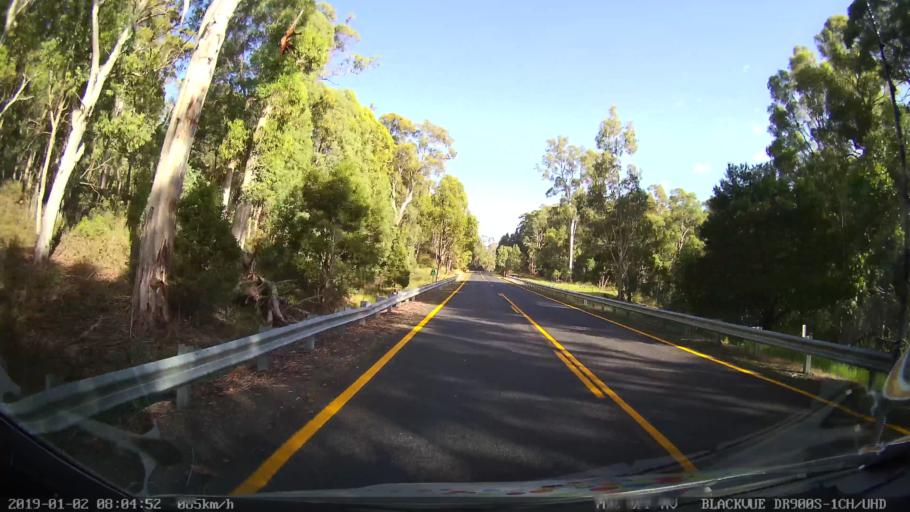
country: AU
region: New South Wales
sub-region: Tumut Shire
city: Tumut
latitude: -35.6579
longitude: 148.3911
